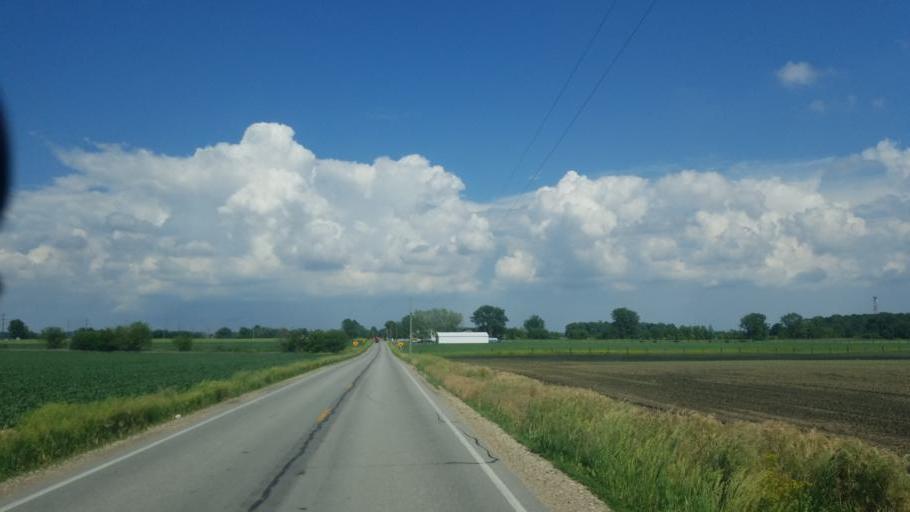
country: US
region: Indiana
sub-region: Marshall County
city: Bourbon
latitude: 41.3144
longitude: -86.0451
